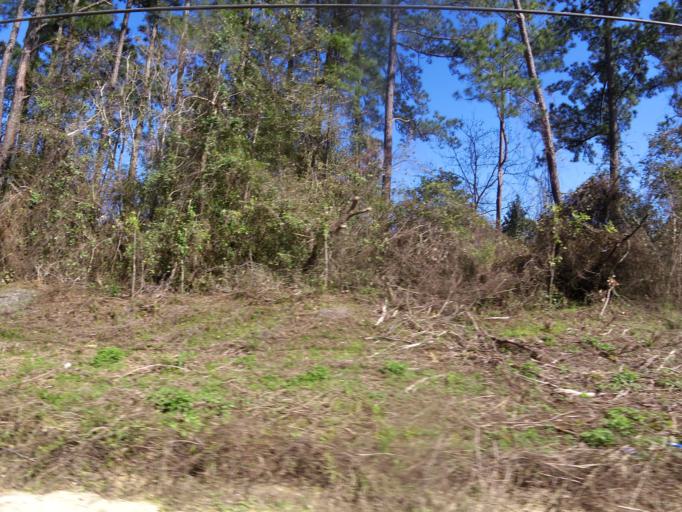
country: US
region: Florida
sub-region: Clay County
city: Middleburg
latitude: 30.1245
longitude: -81.8818
